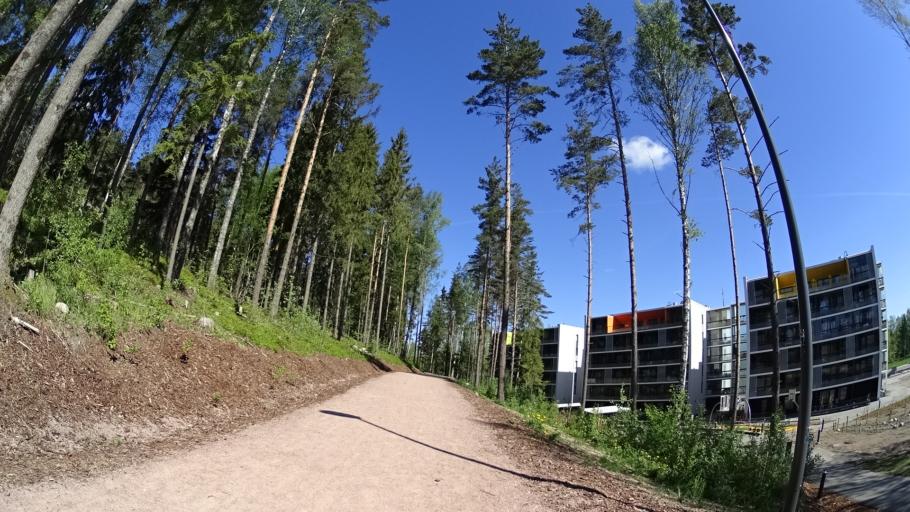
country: FI
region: Uusimaa
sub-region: Helsinki
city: Espoo
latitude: 60.1658
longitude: 24.6224
